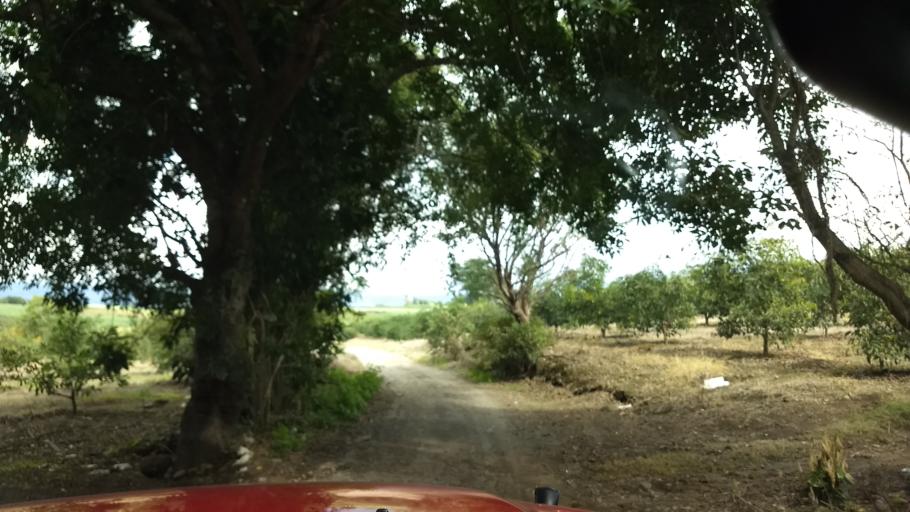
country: MX
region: Colima
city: Suchitlan
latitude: 19.4623
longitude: -103.7511
